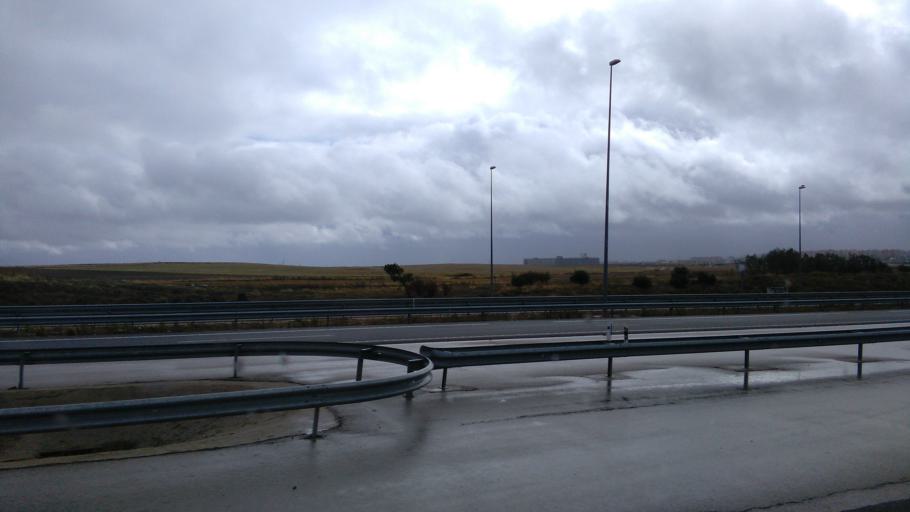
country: ES
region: Madrid
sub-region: Provincia de Madrid
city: Alcorcon
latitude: 40.3235
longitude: -3.8182
